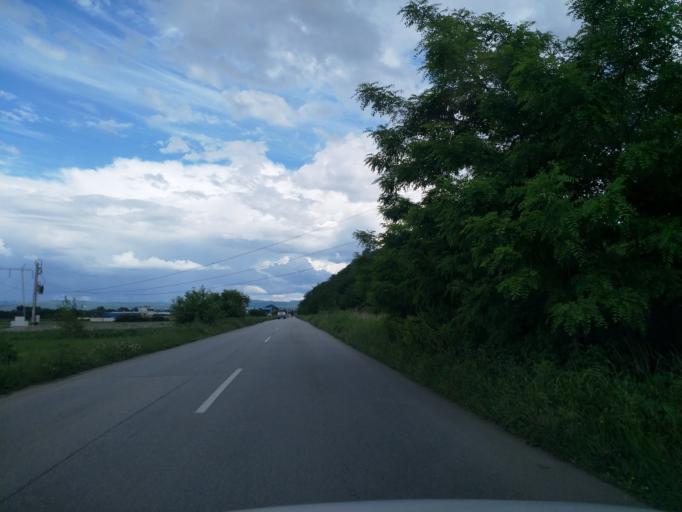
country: RS
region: Central Serbia
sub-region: Pomoravski Okrug
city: Jagodina
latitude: 43.9547
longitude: 21.3095
